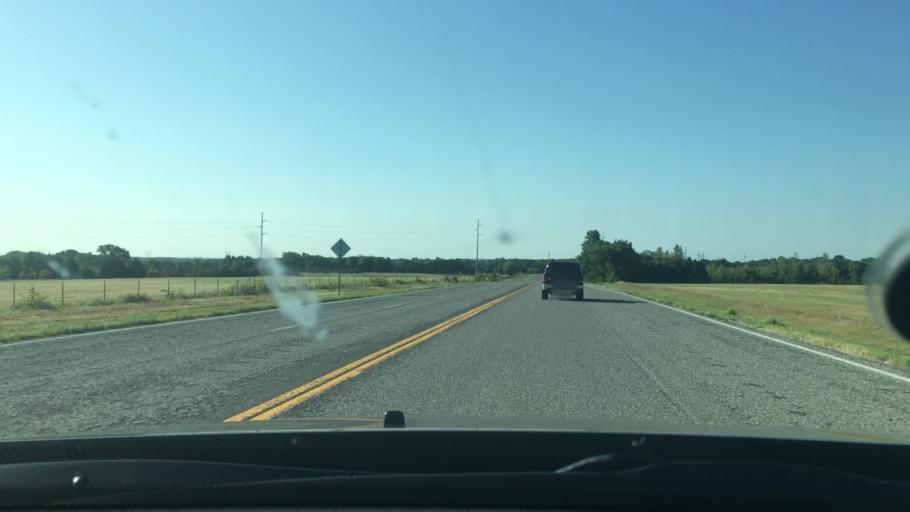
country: US
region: Oklahoma
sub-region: Johnston County
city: Tishomingo
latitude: 34.2773
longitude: -96.7782
